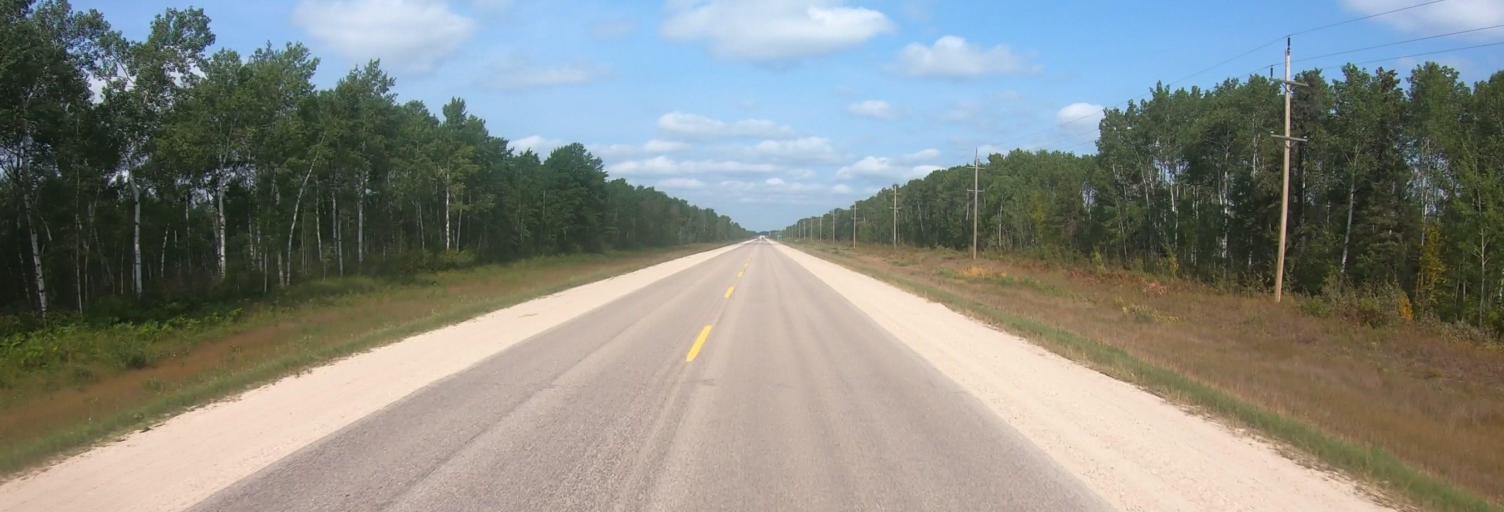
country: CA
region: Manitoba
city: La Broquerie
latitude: 49.1958
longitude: -96.2645
